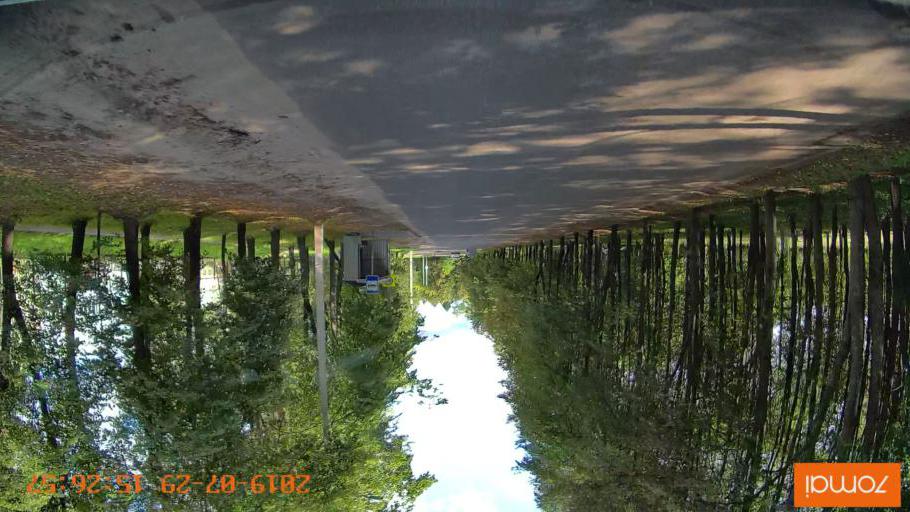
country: RU
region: Ivanovo
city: Bogorodskoye
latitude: 57.0190
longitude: 41.0056
